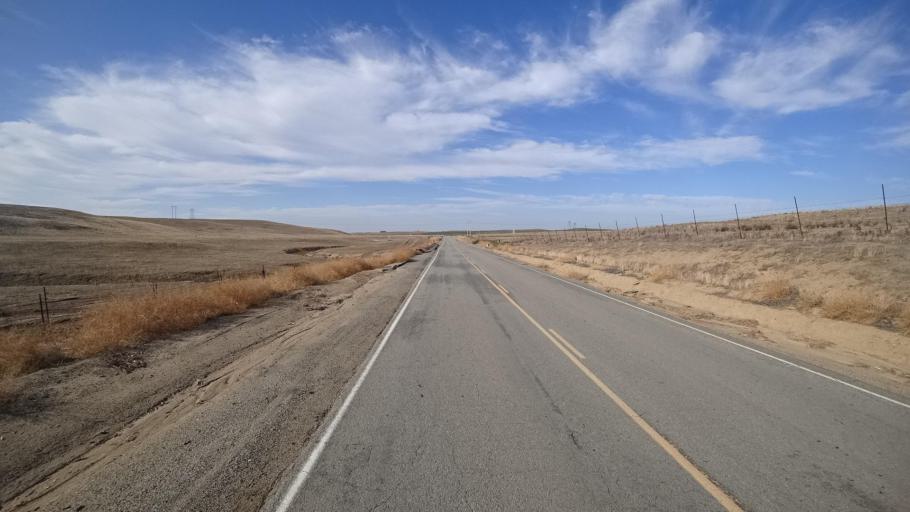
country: US
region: California
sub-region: Tulare County
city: Richgrove
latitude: 35.6208
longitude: -119.0342
